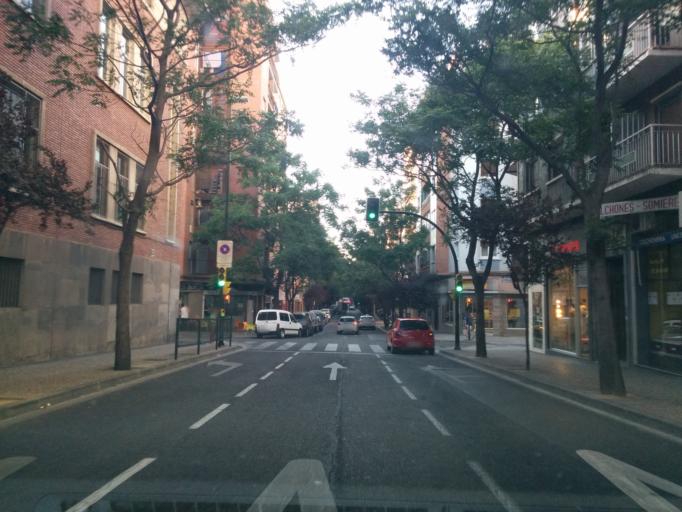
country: ES
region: Aragon
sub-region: Provincia de Zaragoza
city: Delicias
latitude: 41.6492
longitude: -0.9006
